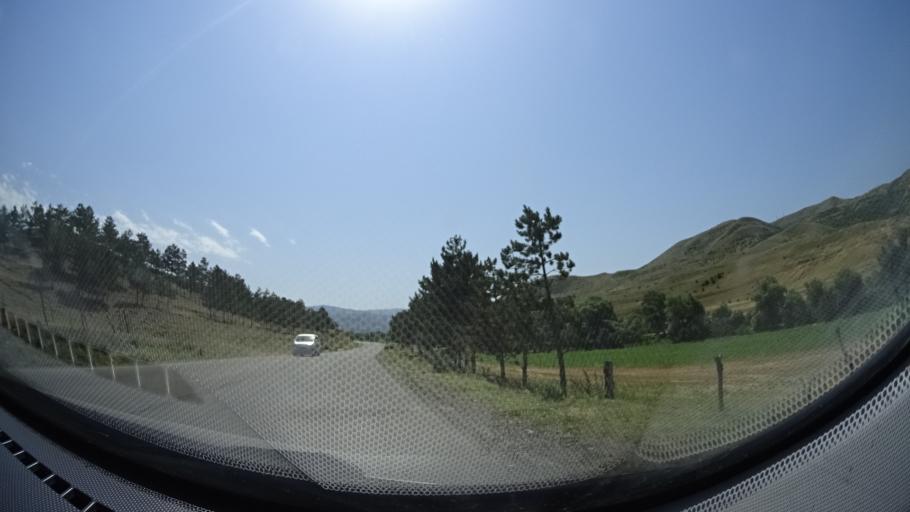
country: GE
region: Samtskhe-Javakheti
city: Aspindza
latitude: 41.5964
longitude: 43.2084
